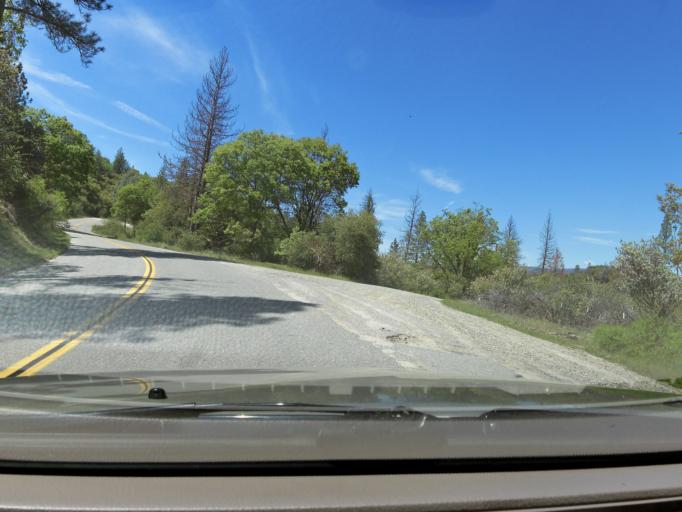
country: US
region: California
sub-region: Fresno County
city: Auberry
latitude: 37.2336
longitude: -119.5138
